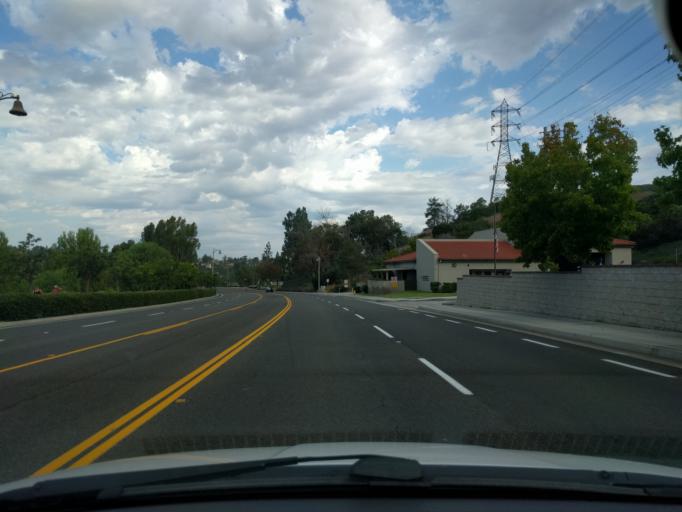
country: US
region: California
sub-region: Orange County
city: Rancho Santa Margarita
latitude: 33.6361
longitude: -117.6373
